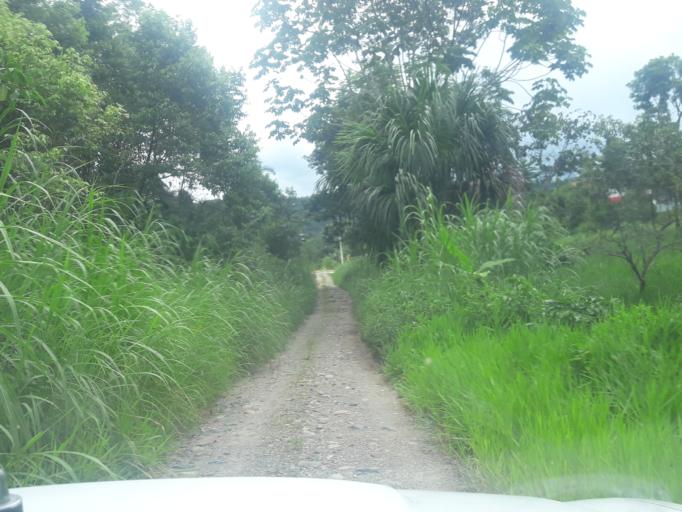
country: EC
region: Napo
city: Tena
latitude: -0.9567
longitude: -77.8144
